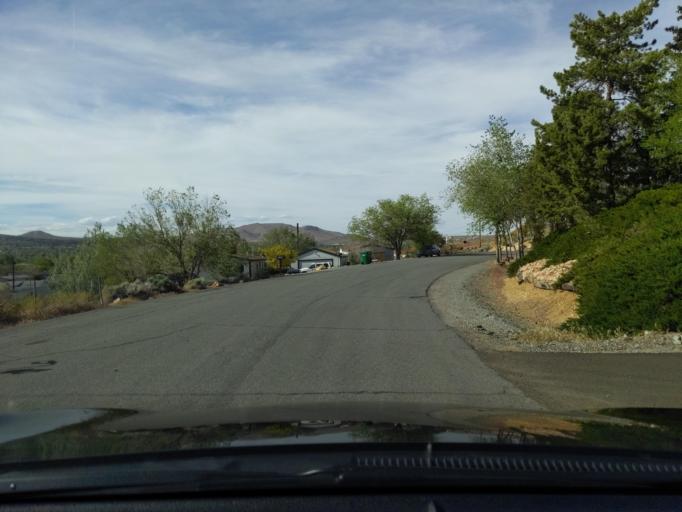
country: US
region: Nevada
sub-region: Washoe County
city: Sun Valley
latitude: 39.5841
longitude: -119.7716
